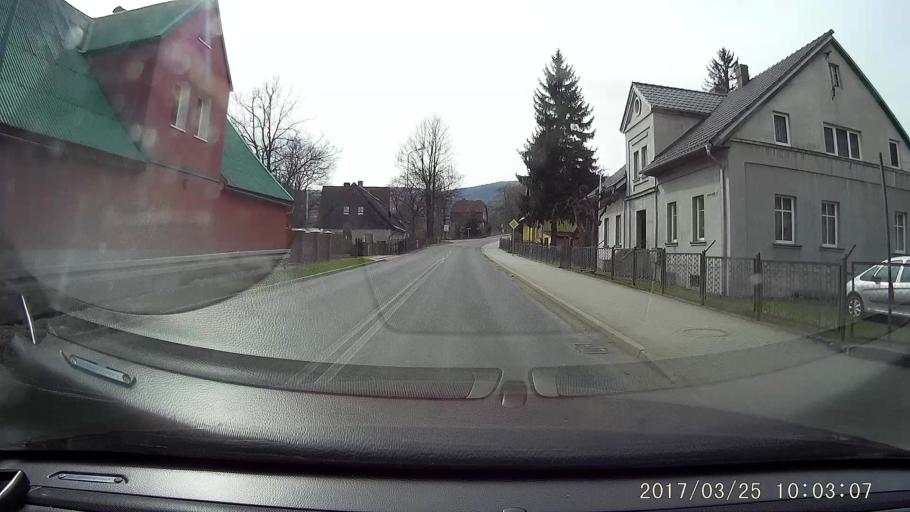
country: PL
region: Lower Silesian Voivodeship
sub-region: Powiat lubanski
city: Swieradow-Zdroj
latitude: 50.9162
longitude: 15.3417
